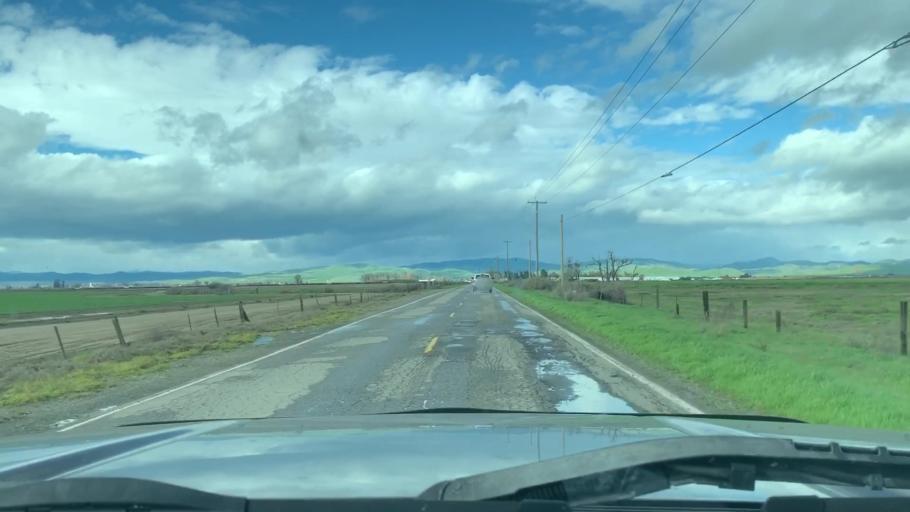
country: US
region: California
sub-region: Merced County
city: Los Banos
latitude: 37.1220
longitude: -120.9532
